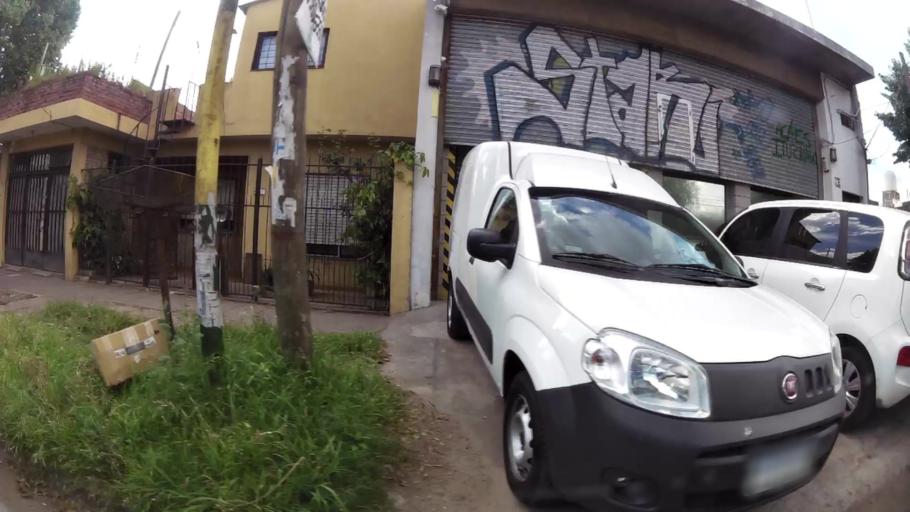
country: AR
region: Buenos Aires
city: Ituzaingo
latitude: -34.6366
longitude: -58.6695
